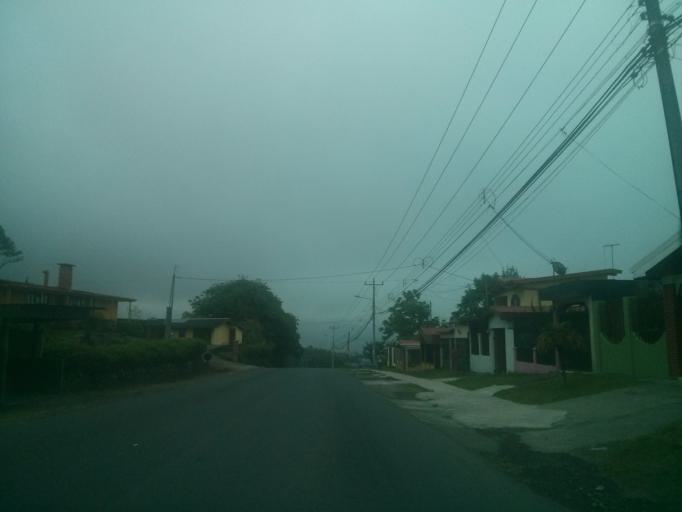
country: CR
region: Cartago
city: Cot
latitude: 9.8823
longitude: -83.8136
